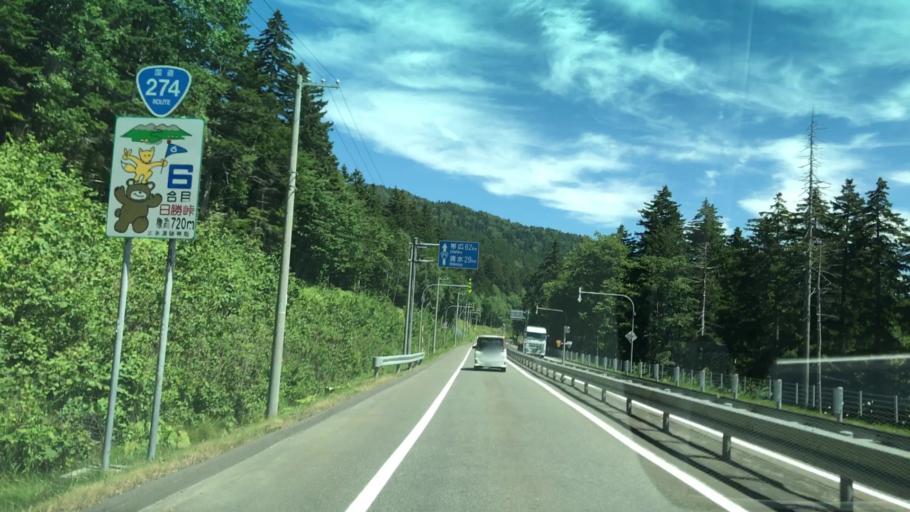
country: JP
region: Hokkaido
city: Shimo-furano
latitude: 42.9692
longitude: 142.6748
